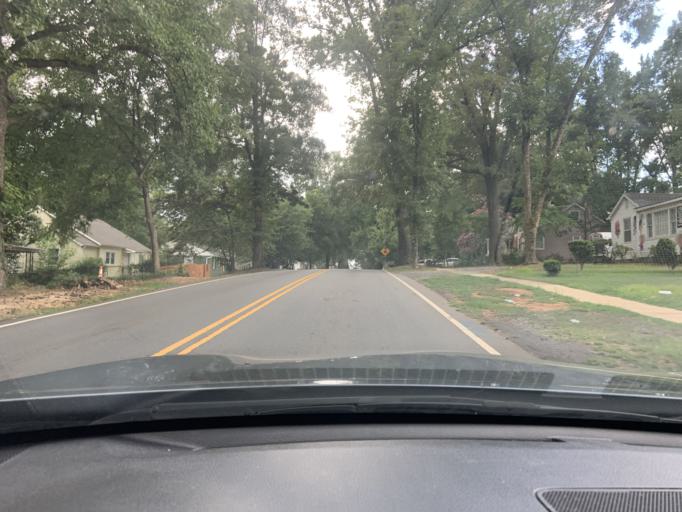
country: US
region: North Carolina
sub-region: Mecklenburg County
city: Charlotte
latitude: 35.2295
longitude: -80.8843
